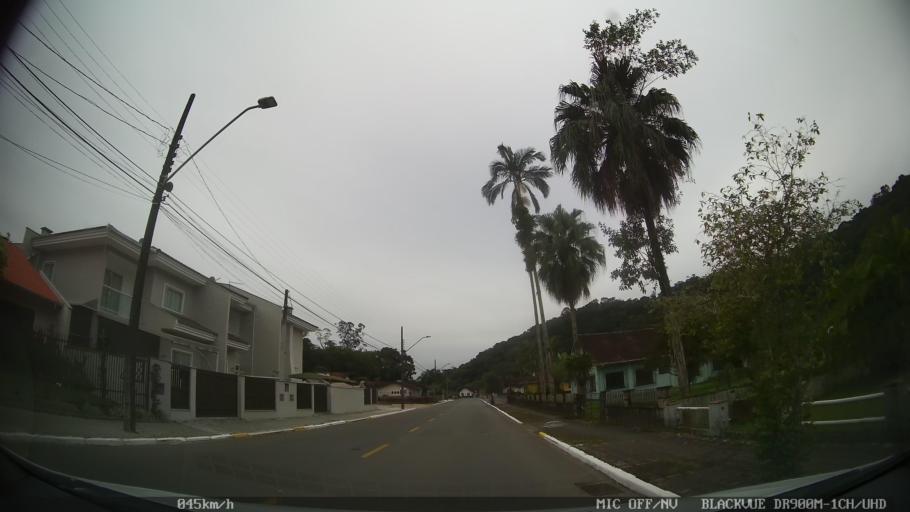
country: BR
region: Santa Catarina
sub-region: Joinville
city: Joinville
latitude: -26.2148
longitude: -48.9118
